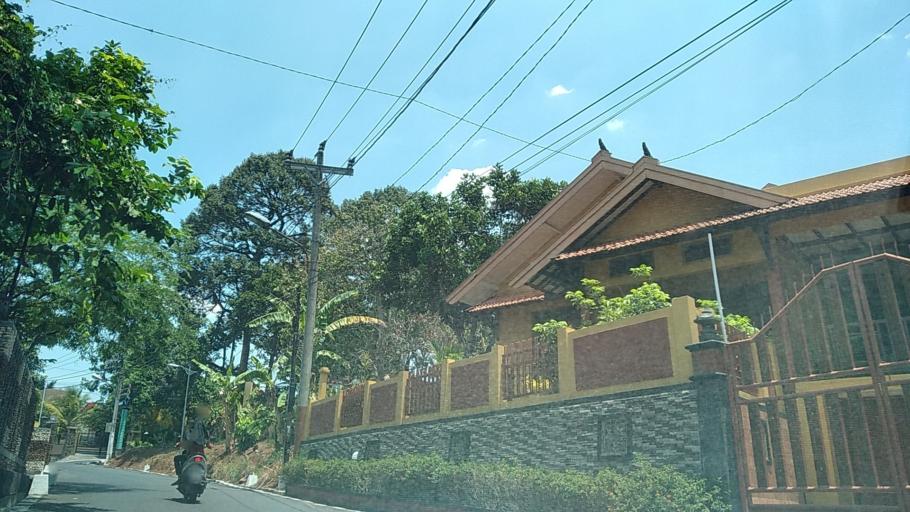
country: ID
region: Central Java
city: Ungaran
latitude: -7.0781
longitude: 110.4296
